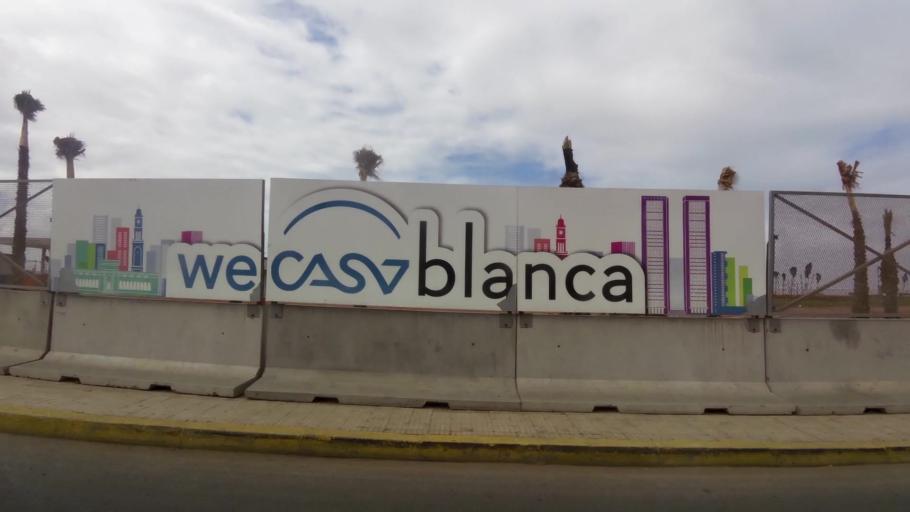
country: MA
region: Grand Casablanca
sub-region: Casablanca
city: Casablanca
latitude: 33.6040
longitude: -7.6387
